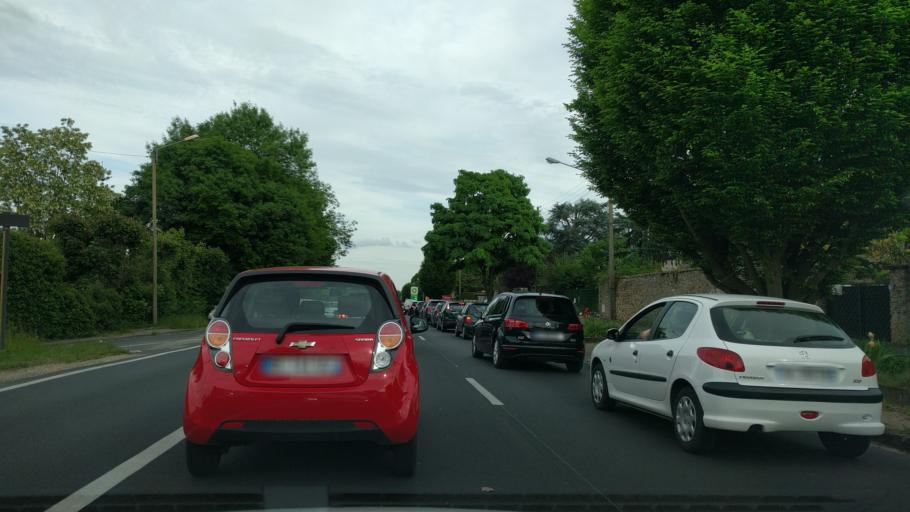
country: FR
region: Ile-de-France
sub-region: Departement de Seine-et-Marne
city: Ponthierry
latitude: 48.5348
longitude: 2.5310
